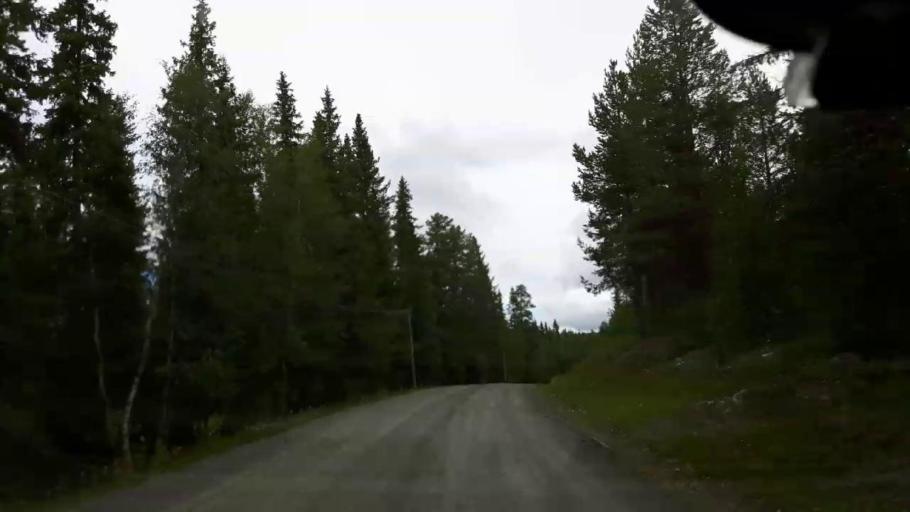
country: SE
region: Jaemtland
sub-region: Krokoms Kommun
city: Valla
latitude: 63.6904
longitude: 13.8676
